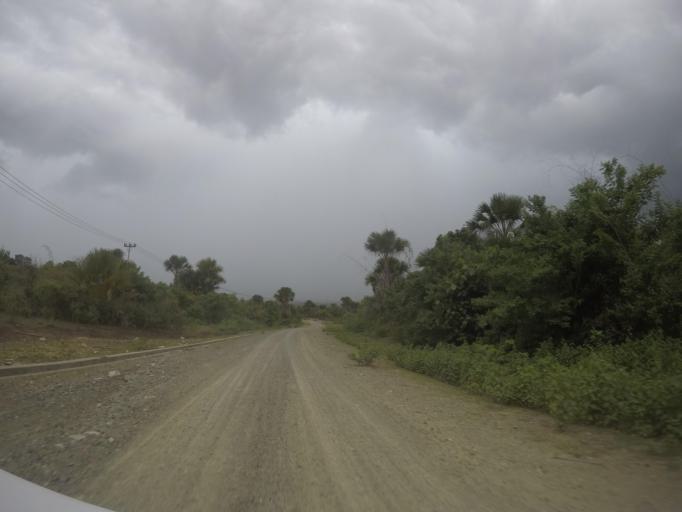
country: TL
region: Bobonaro
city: Maliana
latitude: -8.8540
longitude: 125.0767
